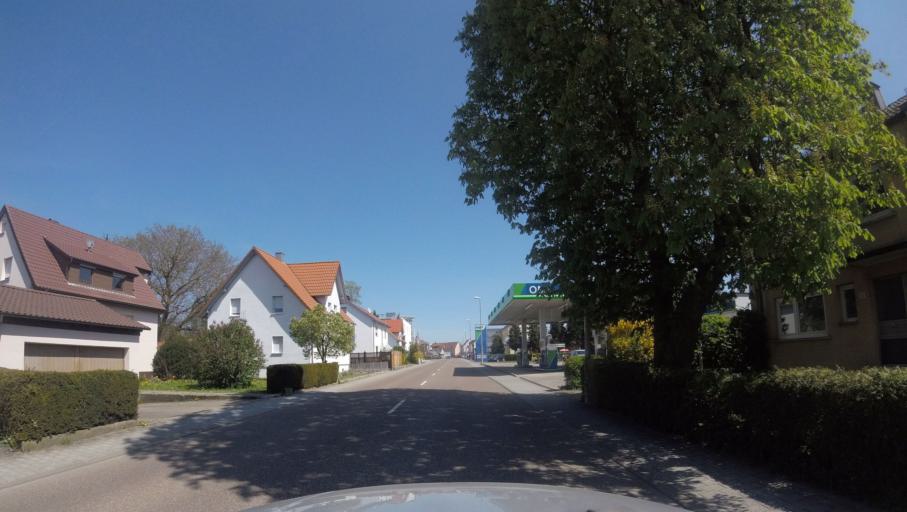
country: DE
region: Baden-Wuerttemberg
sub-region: Regierungsbezirk Stuttgart
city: Mutlangen
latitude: 48.8206
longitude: 9.7942
